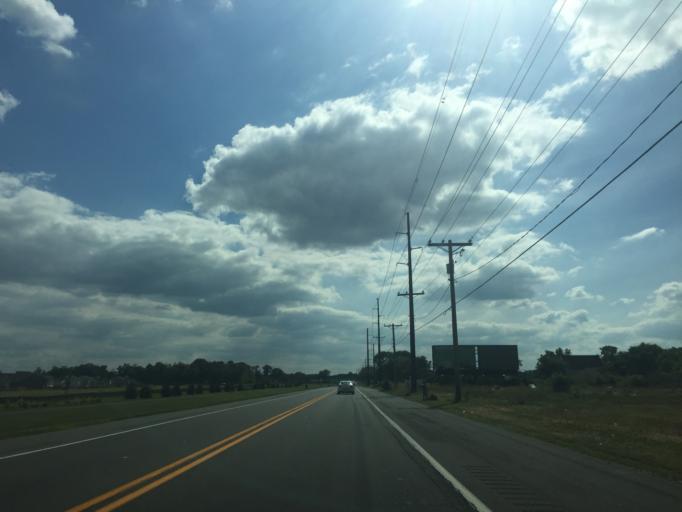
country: US
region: Delaware
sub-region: Sussex County
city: Lewes
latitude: 38.7451
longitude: -75.1830
